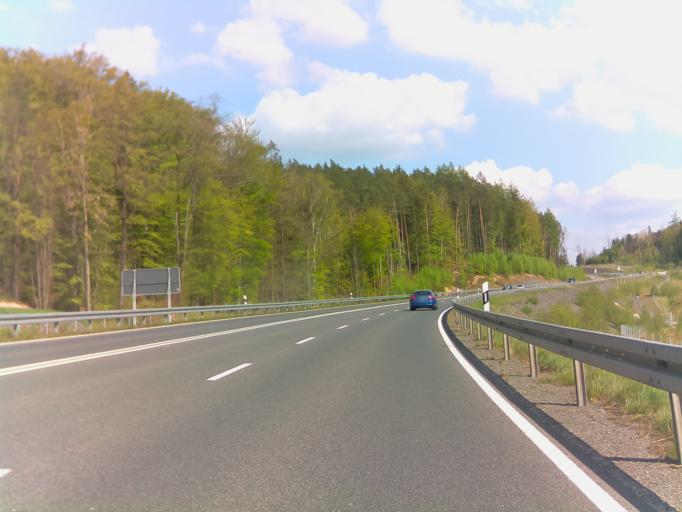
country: DE
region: Bavaria
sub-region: Upper Franconia
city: Rodental
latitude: 50.3085
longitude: 11.0319
